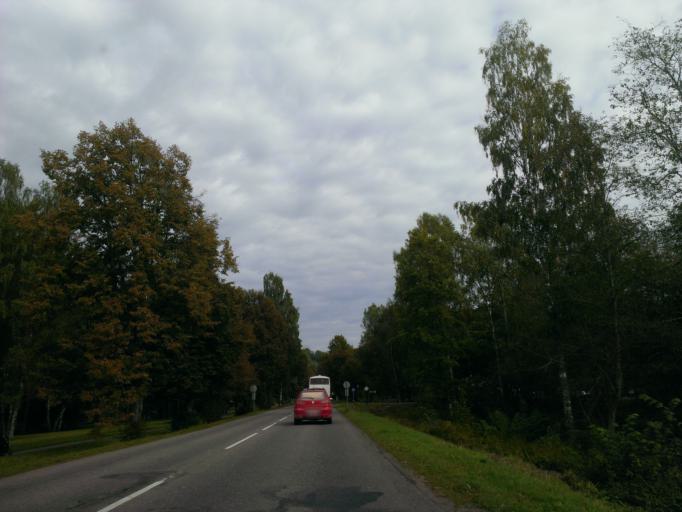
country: LV
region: Sigulda
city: Sigulda
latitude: 57.1753
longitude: 24.8446
